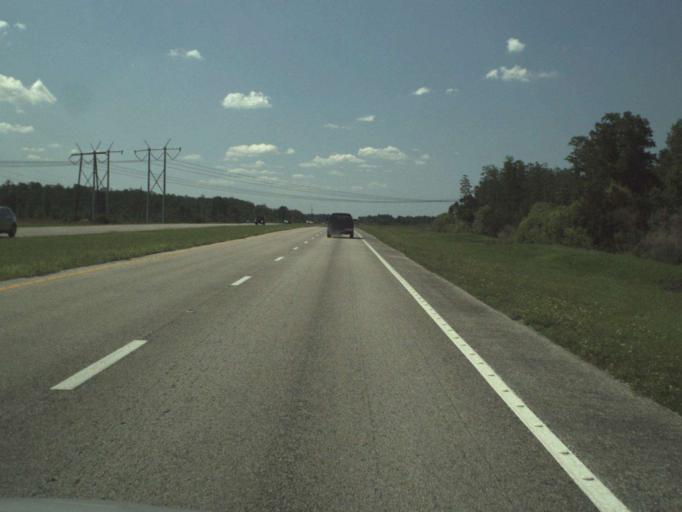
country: US
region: Florida
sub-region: Orange County
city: Wedgefield
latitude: 28.5047
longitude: -81.0536
